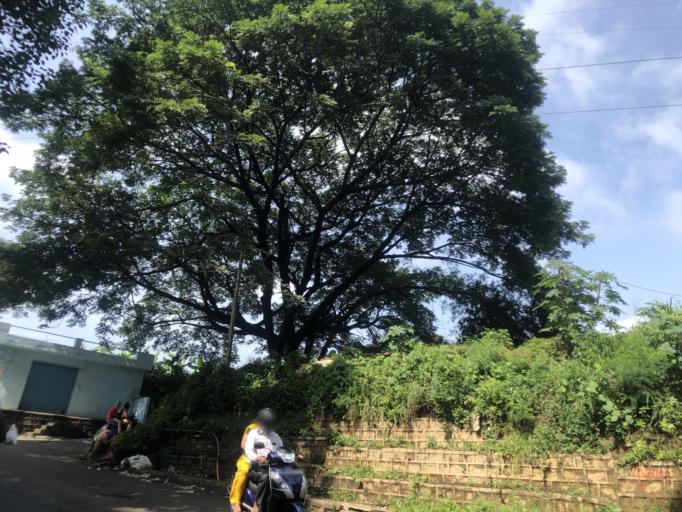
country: IN
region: Karnataka
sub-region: Bangalore Urban
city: Bangalore
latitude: 12.9279
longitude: 77.5315
